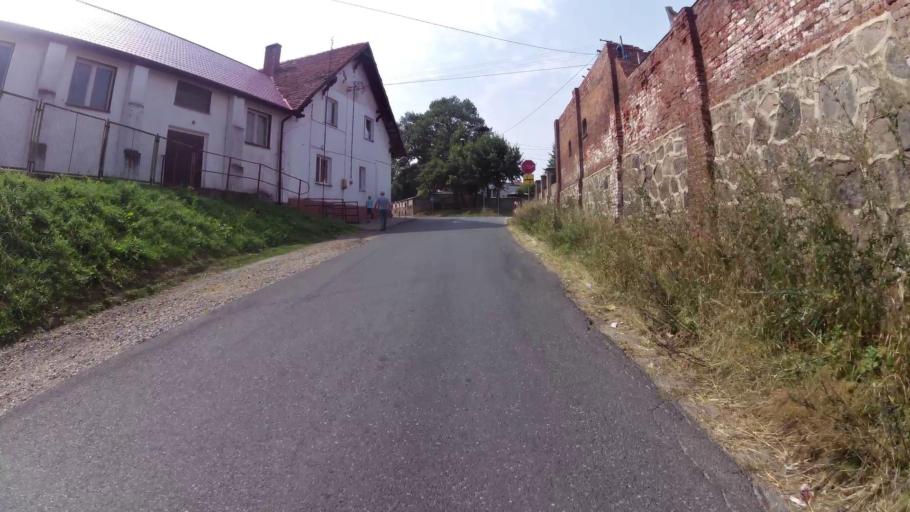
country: PL
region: West Pomeranian Voivodeship
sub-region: Powiat gryfinski
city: Moryn
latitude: 52.8706
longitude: 14.4752
